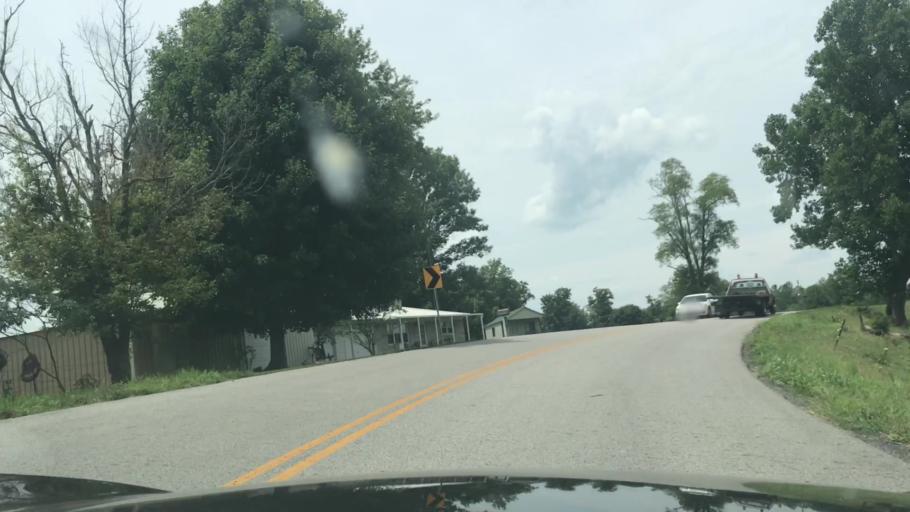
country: US
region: Kentucky
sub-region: Green County
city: Greensburg
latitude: 37.2689
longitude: -85.5333
